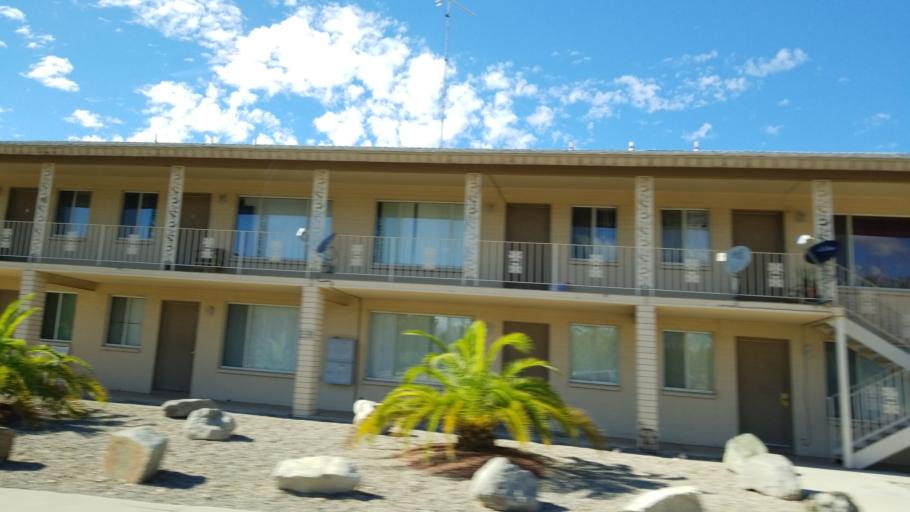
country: US
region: Arizona
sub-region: Mohave County
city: Lake Havasu City
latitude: 34.4781
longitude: -114.3193
